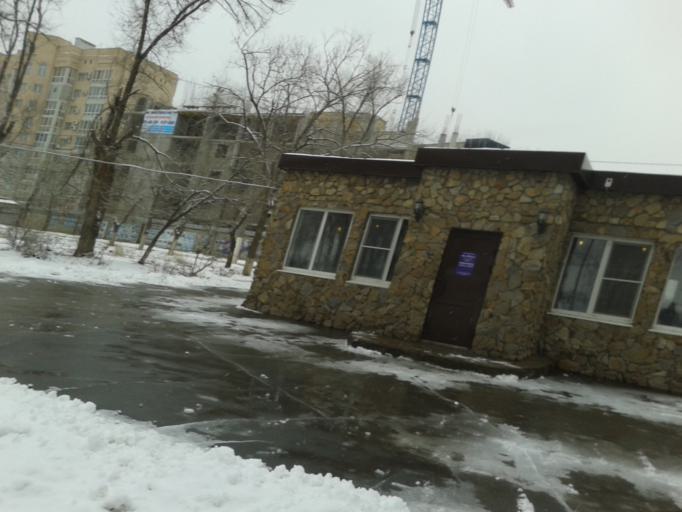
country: RU
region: Volgograd
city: Krasnoslobodsk
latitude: 48.5275
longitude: 44.5605
